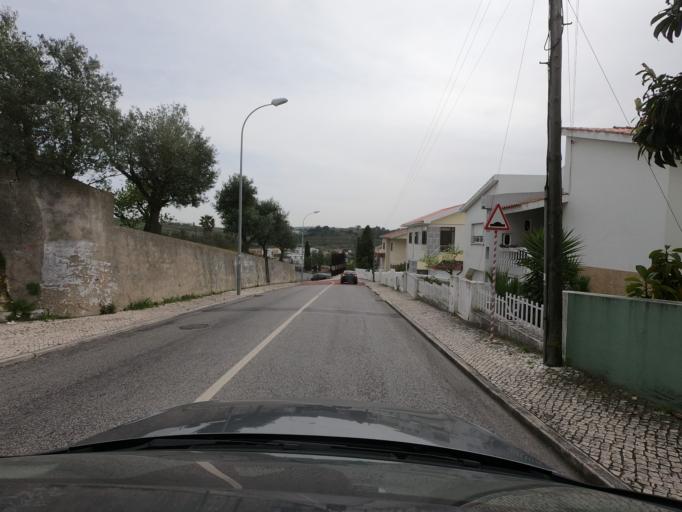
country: PT
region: Lisbon
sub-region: Oeiras
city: Barcarena
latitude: 38.7286
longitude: -9.2831
